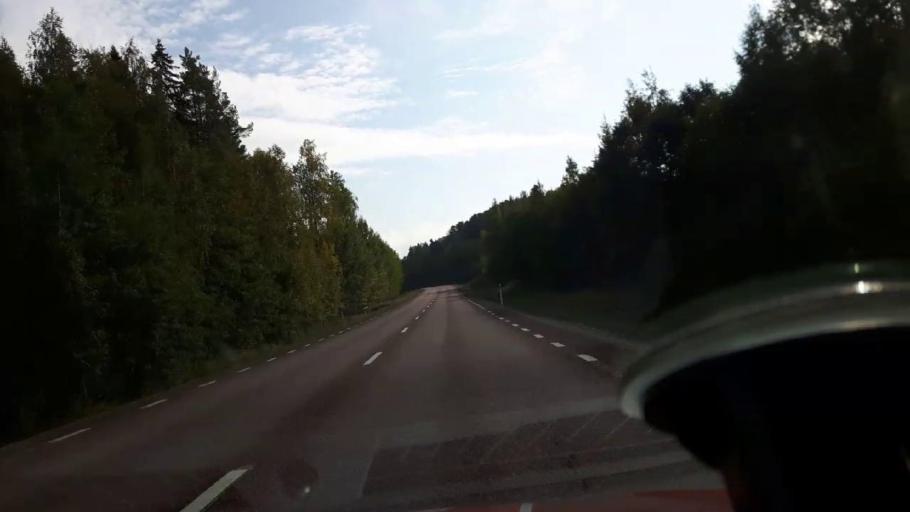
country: SE
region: Gaevleborg
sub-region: Bollnas Kommun
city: Kilafors
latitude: 61.2082
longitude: 16.7438
